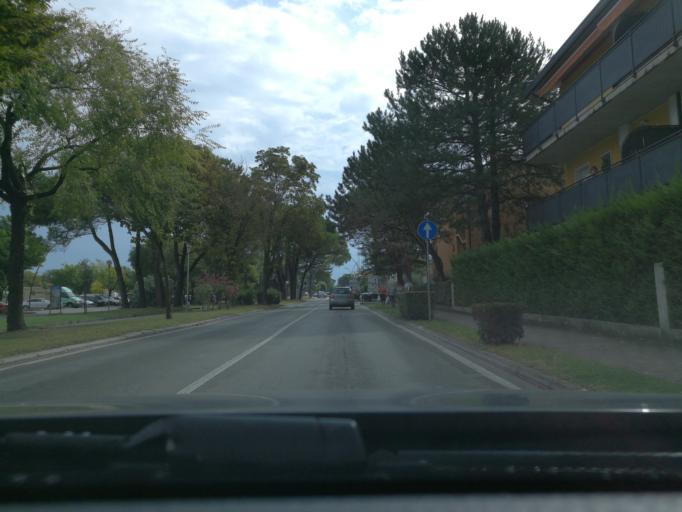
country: IT
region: Veneto
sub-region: Provincia di Venezia
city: Bibione
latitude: 45.6381
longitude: 13.0522
